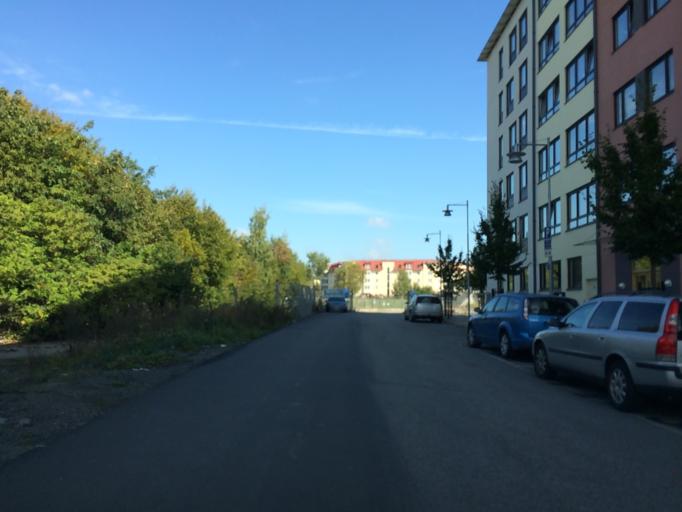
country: SE
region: Stockholm
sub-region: Stockholms Kommun
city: Arsta
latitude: 59.2975
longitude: 17.9983
